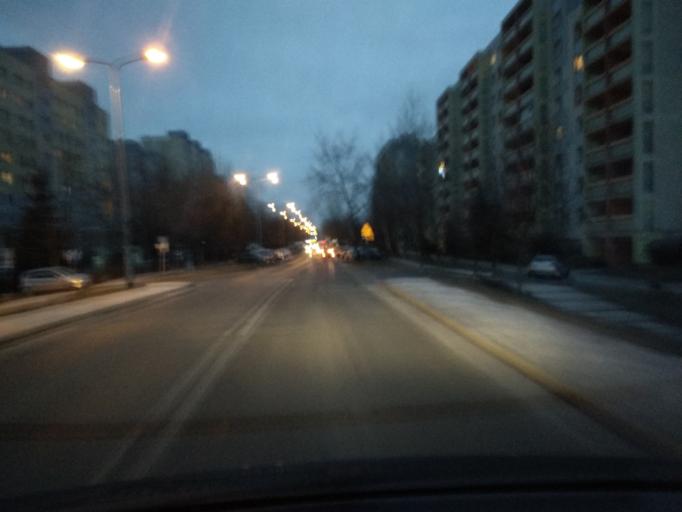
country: PL
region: Lower Silesian Voivodeship
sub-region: Powiat wroclawski
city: Wroclaw
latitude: 51.1257
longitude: 16.9621
